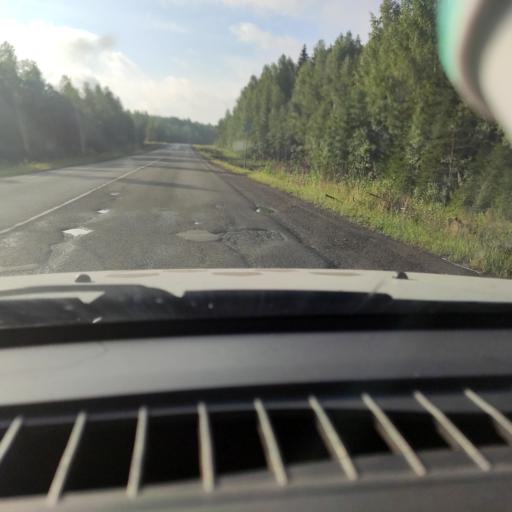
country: RU
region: Kirov
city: Omutninsk
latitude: 58.7522
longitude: 52.0513
